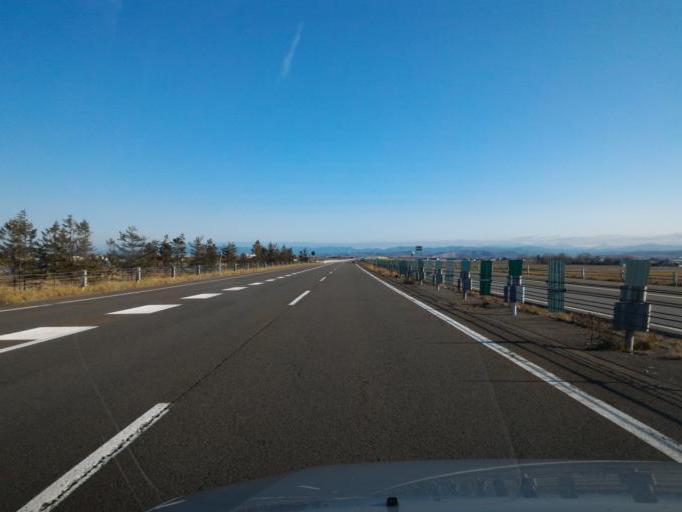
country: JP
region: Hokkaido
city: Iwamizawa
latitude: 43.1431
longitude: 141.6779
